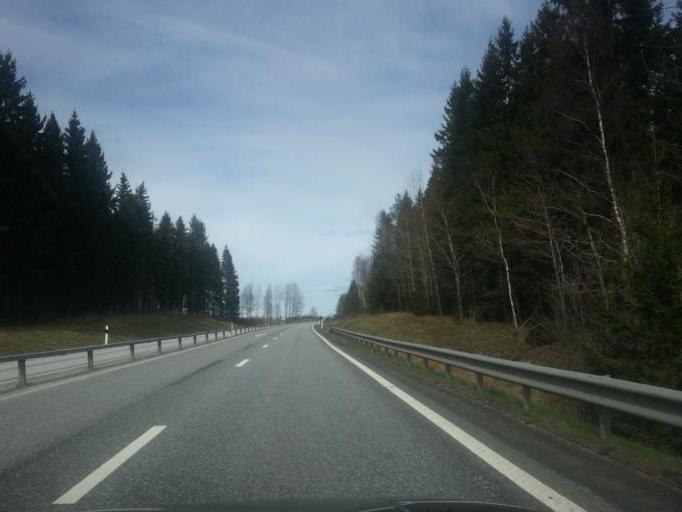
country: SE
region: Joenkoeping
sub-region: Jonkopings Kommun
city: Bankeryd
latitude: 57.8341
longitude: 14.1015
